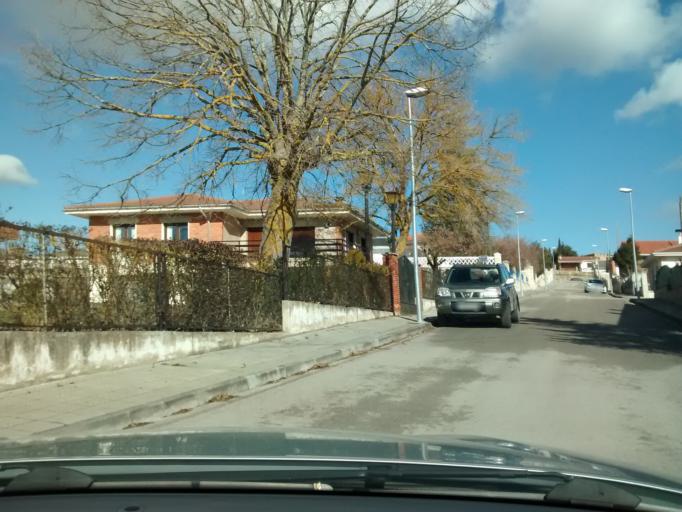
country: ES
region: Castille and Leon
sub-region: Provincia de Burgos
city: Medina de Pomar
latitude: 42.9246
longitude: -3.4906
